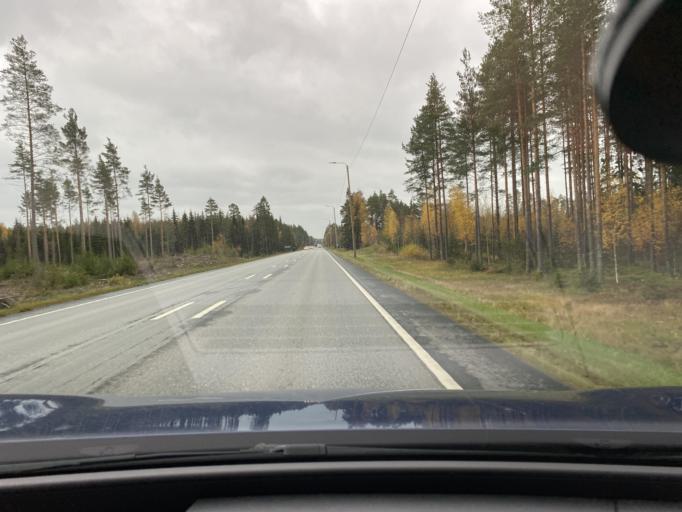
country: FI
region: Varsinais-Suomi
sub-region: Vakka-Suomi
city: Laitila
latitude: 60.9539
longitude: 21.5971
